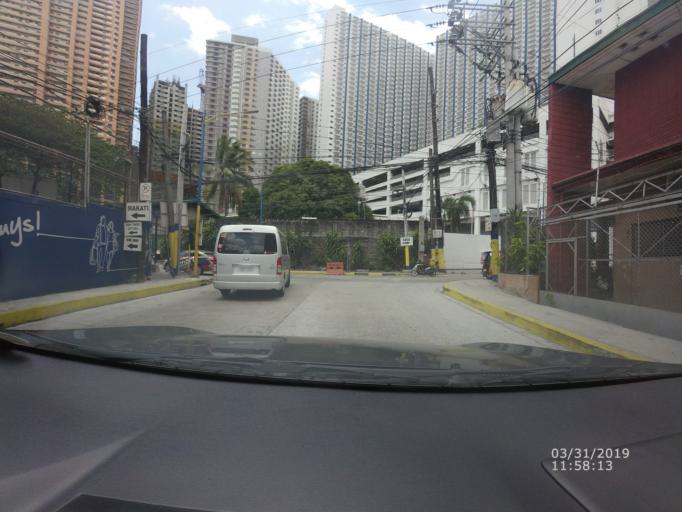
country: PH
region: Metro Manila
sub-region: Mandaluyong
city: Mandaluyong City
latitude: 14.5736
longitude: 121.0502
